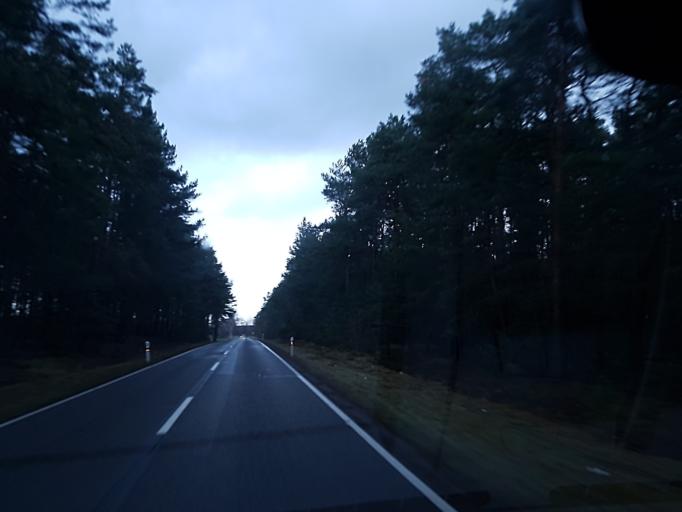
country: DE
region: Brandenburg
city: Finsterwalde
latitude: 51.5544
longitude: 13.6722
